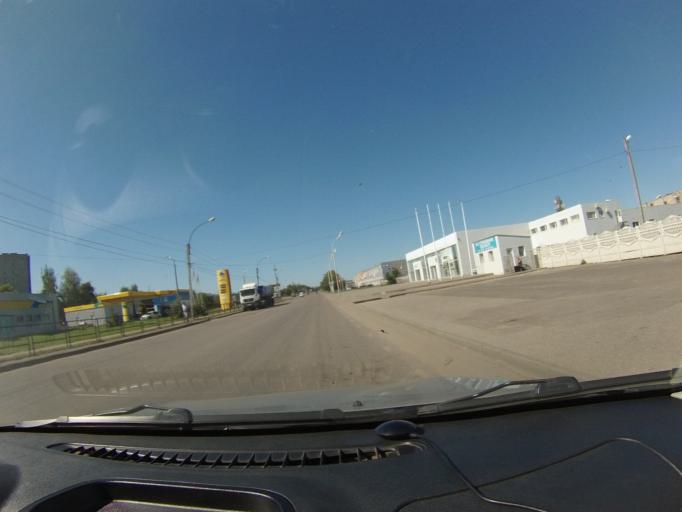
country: RU
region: Tambov
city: Donskoye
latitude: 52.7582
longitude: 41.4723
